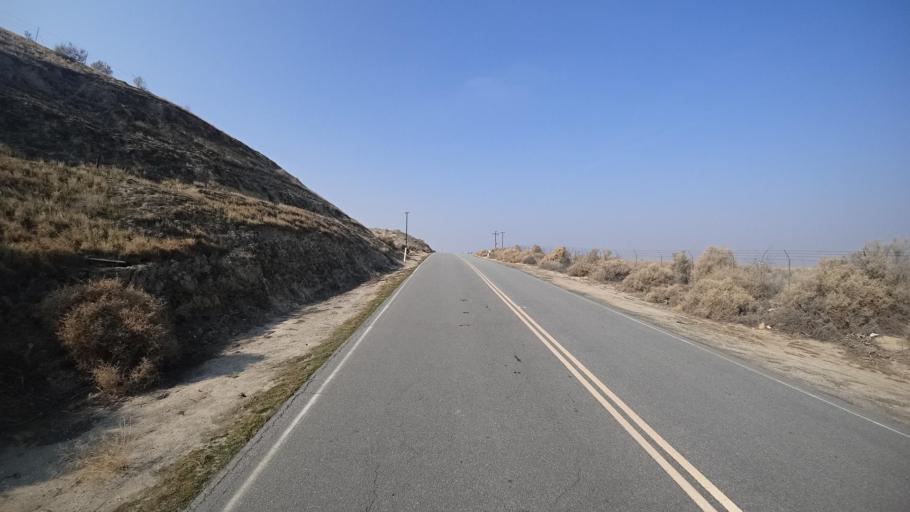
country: US
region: California
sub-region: Kern County
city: Buttonwillow
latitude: 35.2898
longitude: -119.3421
